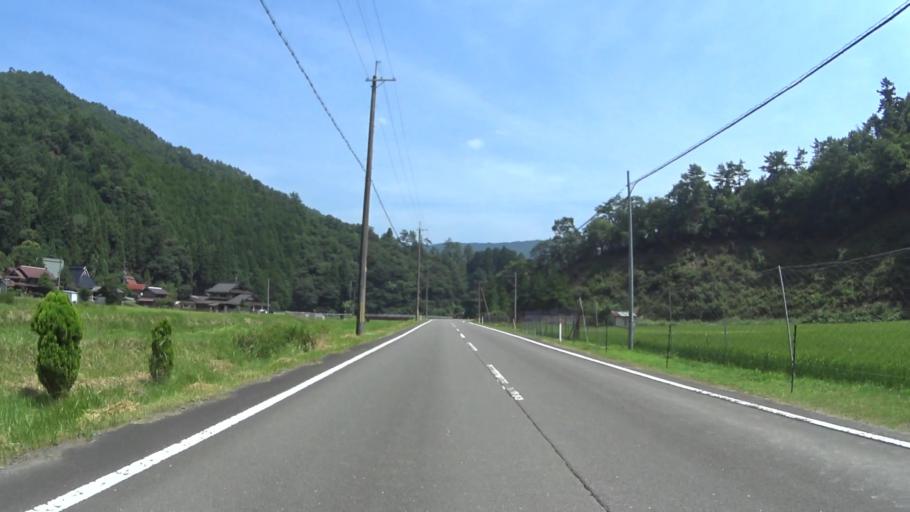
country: JP
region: Kyoto
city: Maizuru
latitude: 35.3298
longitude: 135.5466
